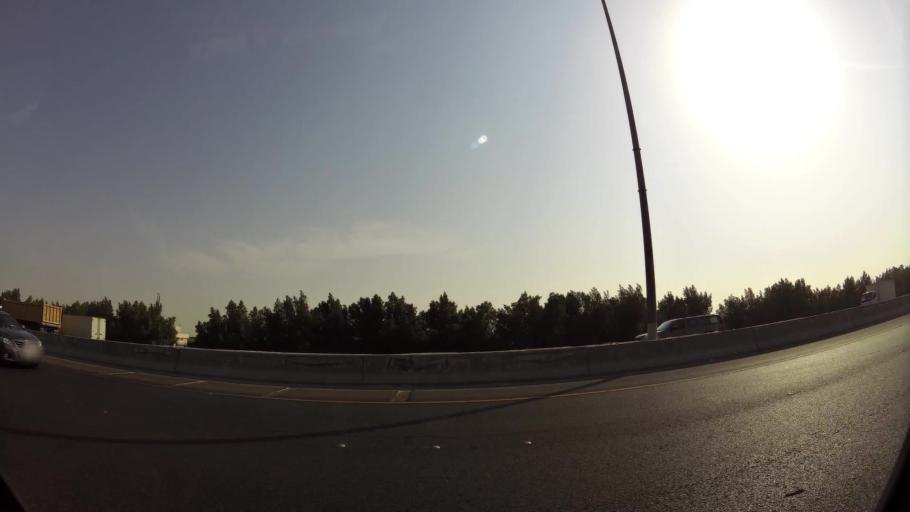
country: KW
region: Al Ahmadi
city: Ar Riqqah
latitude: 29.1108
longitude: 48.0950
